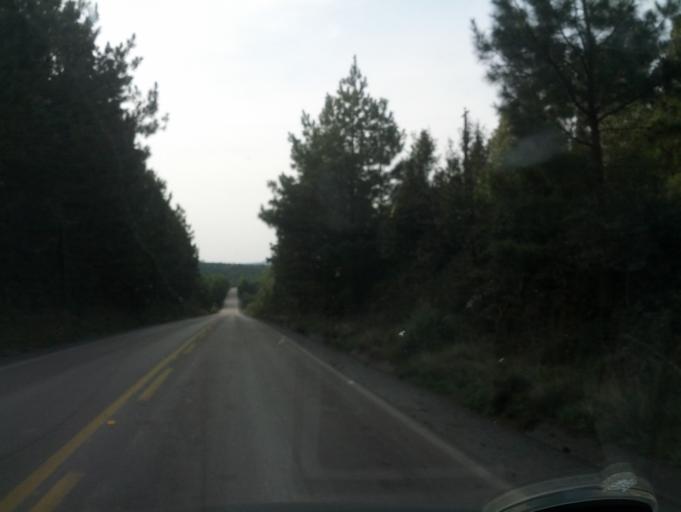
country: BR
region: Santa Catarina
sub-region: Otacilio Costa
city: Otacilio Costa
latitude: -27.3718
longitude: -50.1346
